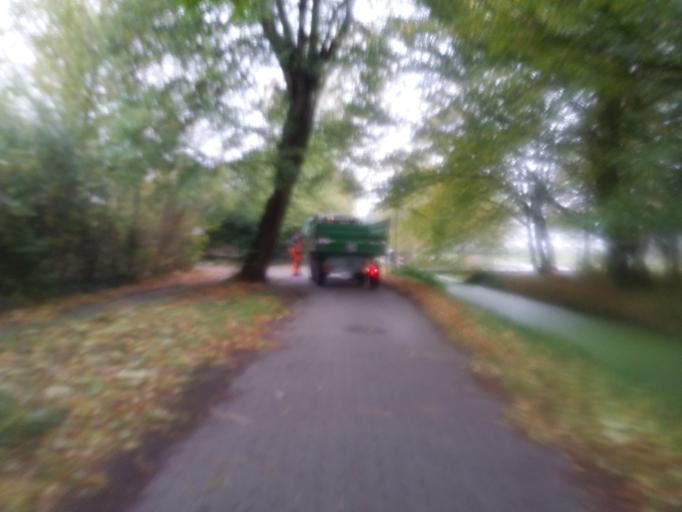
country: DE
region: Bremen
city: Bremen
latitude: 53.0345
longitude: 8.8138
